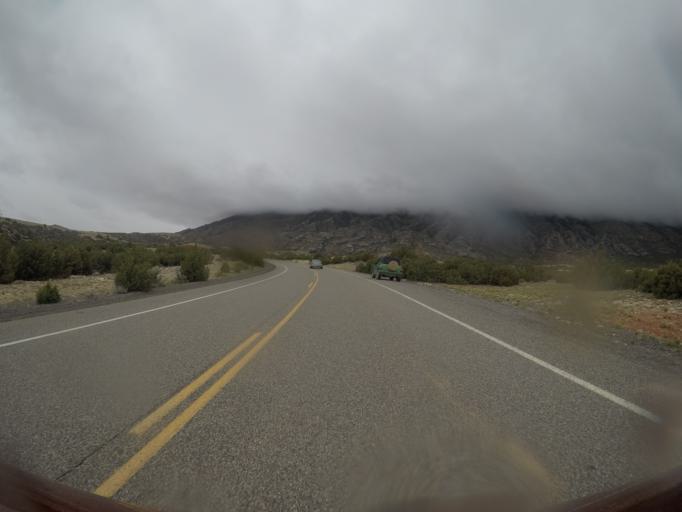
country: US
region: Wyoming
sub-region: Big Horn County
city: Lovell
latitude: 45.0613
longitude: -108.2600
